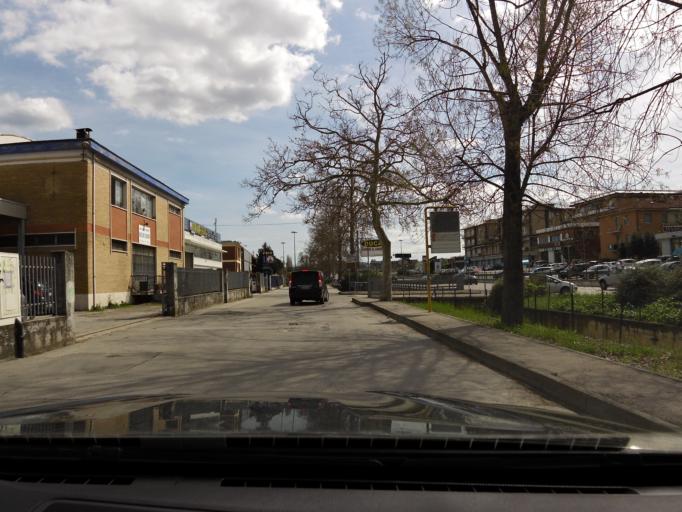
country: IT
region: The Marches
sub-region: Provincia di Ancona
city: Ancona
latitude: 43.5700
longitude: 13.5094
